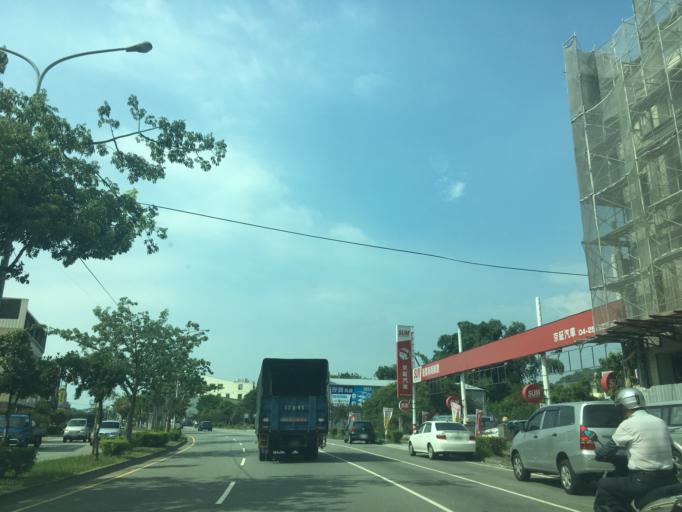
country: TW
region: Taiwan
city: Fengyuan
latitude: 24.2484
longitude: 120.7371
